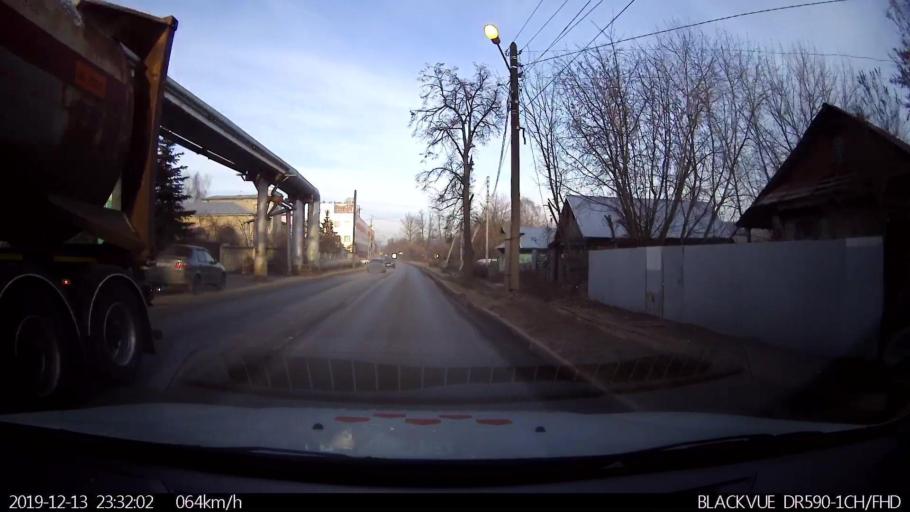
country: RU
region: Nizjnij Novgorod
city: Nizhniy Novgorod
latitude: 56.2714
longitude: 43.9476
